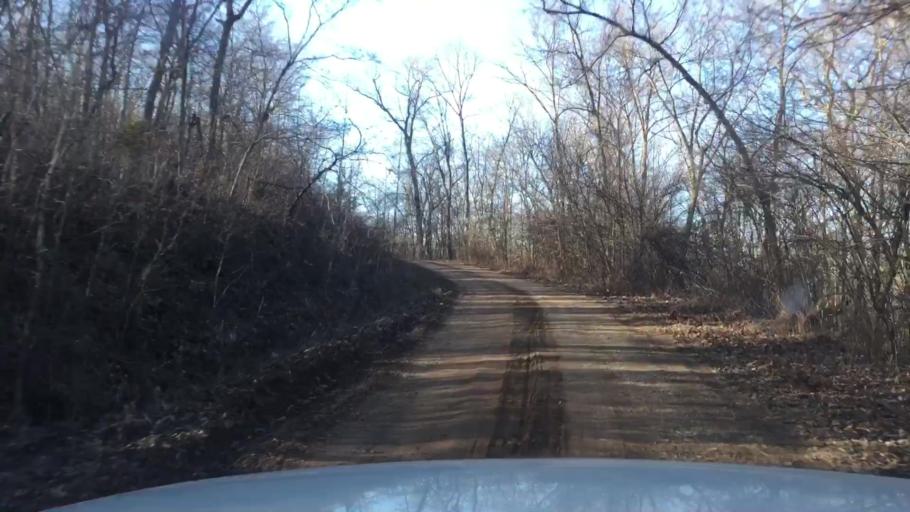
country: US
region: Missouri
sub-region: Morgan County
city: Versailles
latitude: 38.3245
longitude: -92.7675
